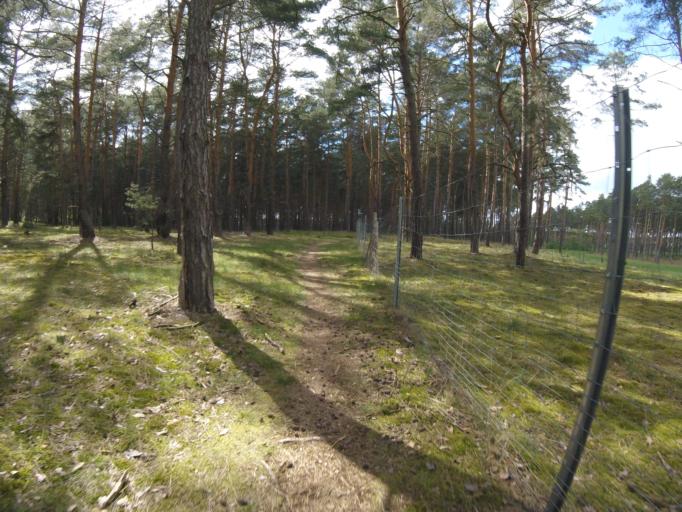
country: DE
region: Brandenburg
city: Schwerin
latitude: 52.1994
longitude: 13.5958
